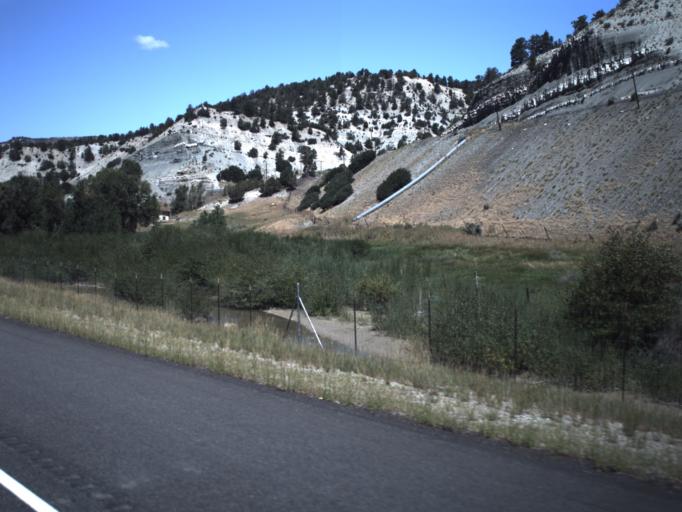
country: US
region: Utah
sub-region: Sanpete County
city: Fairview
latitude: 39.9479
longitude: -111.2137
